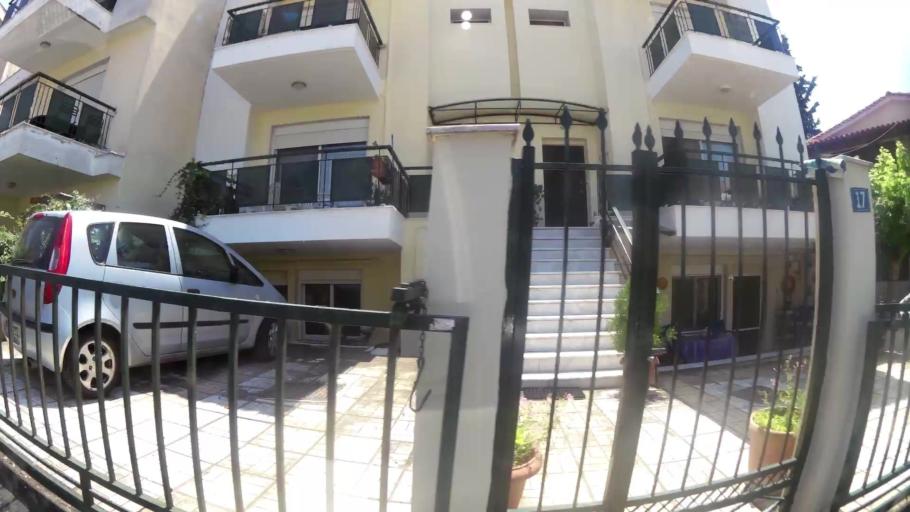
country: GR
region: Central Macedonia
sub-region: Nomos Thessalonikis
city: Trilofos
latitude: 40.4701
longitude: 22.9717
